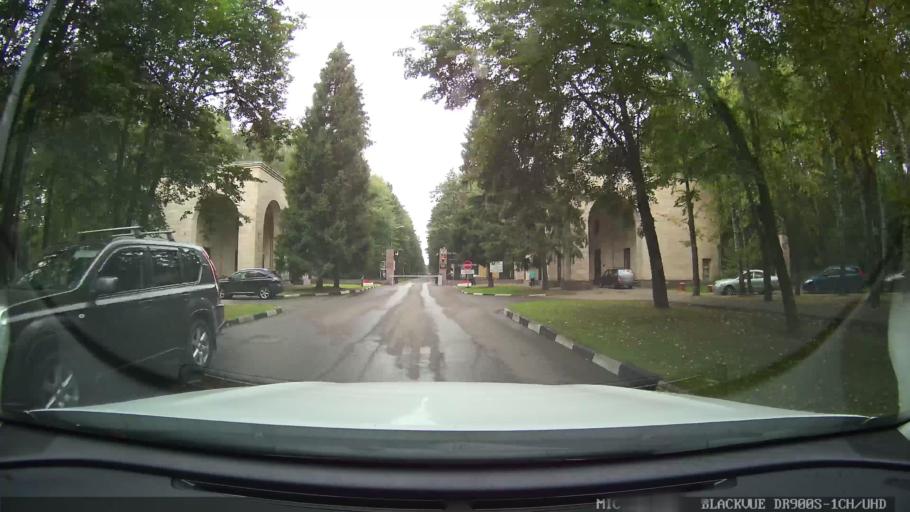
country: RU
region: Moskovskaya
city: Bol'shaya Setun'
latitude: 55.7567
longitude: 37.3930
